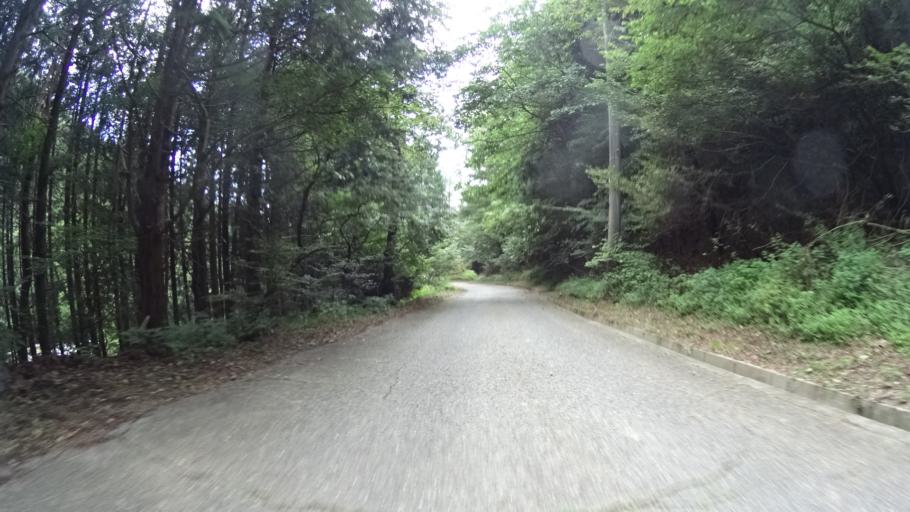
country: JP
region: Yamanashi
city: Nirasaki
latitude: 35.7947
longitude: 138.5290
